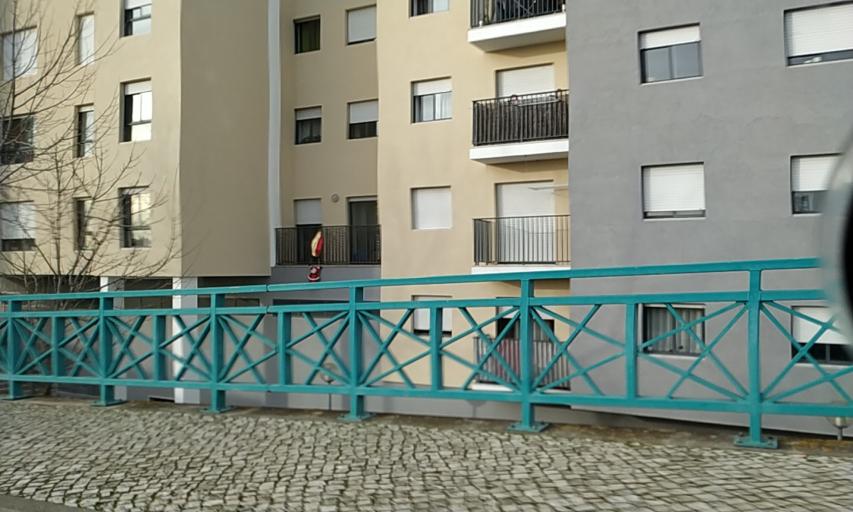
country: PT
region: Setubal
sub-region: Setubal
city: Setubal
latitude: 38.5213
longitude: -8.8752
